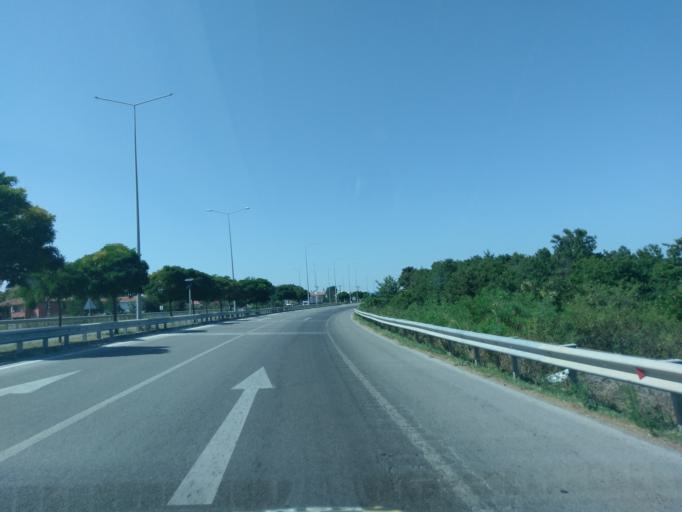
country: TR
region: Samsun
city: Bafra
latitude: 41.5273
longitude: 35.9549
